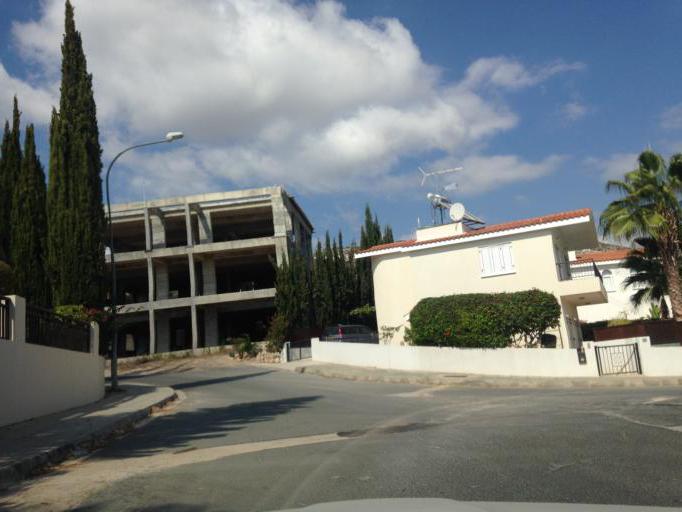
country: CY
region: Pafos
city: Pegeia
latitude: 34.8776
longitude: 32.3682
